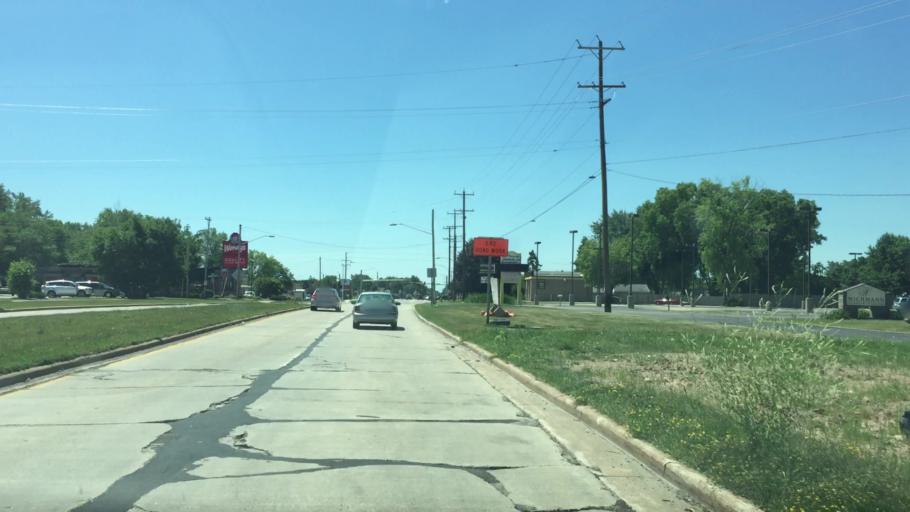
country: US
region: Wisconsin
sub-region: Outagamie County
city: Appleton
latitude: 44.2325
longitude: -88.4041
